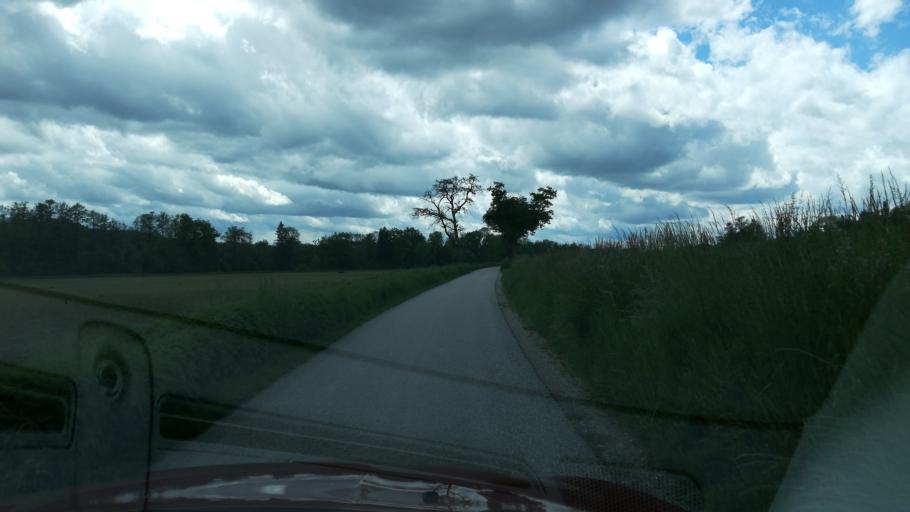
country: AT
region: Upper Austria
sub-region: Politischer Bezirk Linz-Land
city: Traun
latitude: 48.1871
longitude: 14.2249
